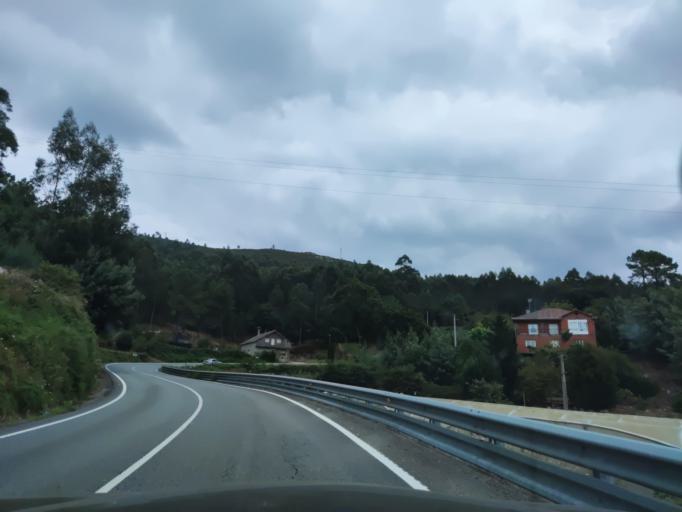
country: ES
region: Galicia
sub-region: Provincia da Coruna
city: Padron
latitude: 42.7393
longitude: -8.6328
